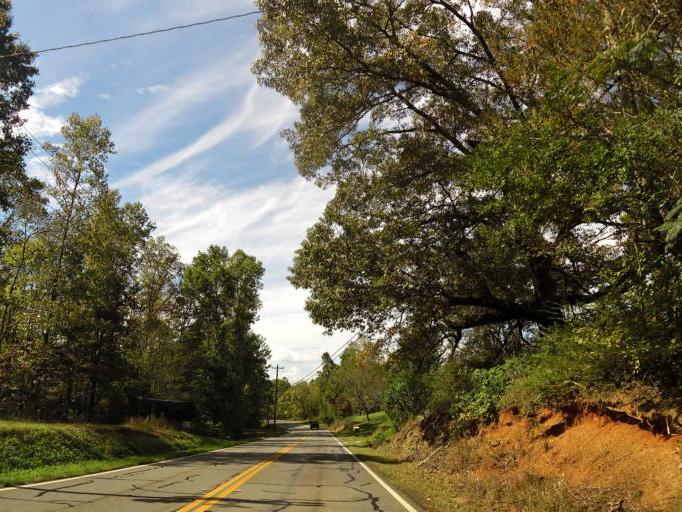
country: US
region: Georgia
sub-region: Pickens County
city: Nelson
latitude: 34.4168
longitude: -84.3010
